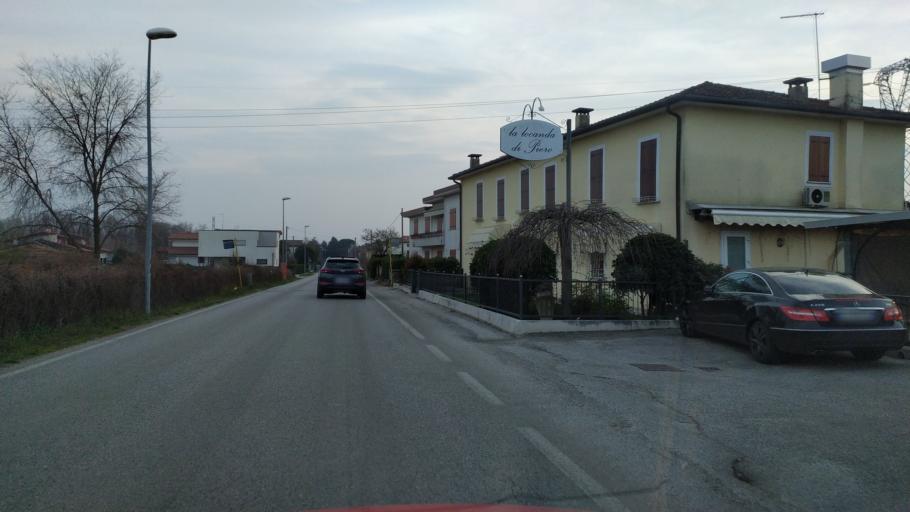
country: IT
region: Veneto
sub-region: Provincia di Vicenza
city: Montecchio Precalcino
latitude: 45.6556
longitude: 11.5581
